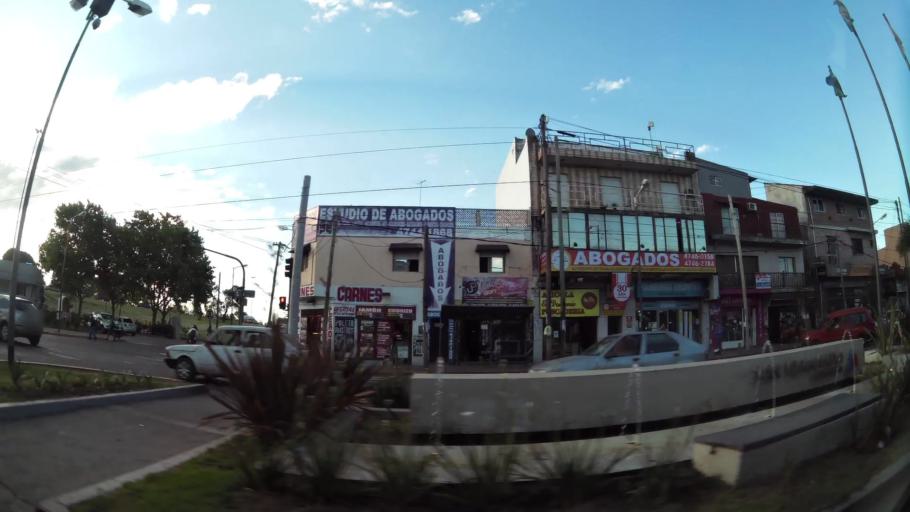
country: AR
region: Buenos Aires
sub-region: Partido de Tigre
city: Tigre
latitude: -34.4602
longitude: -58.5713
